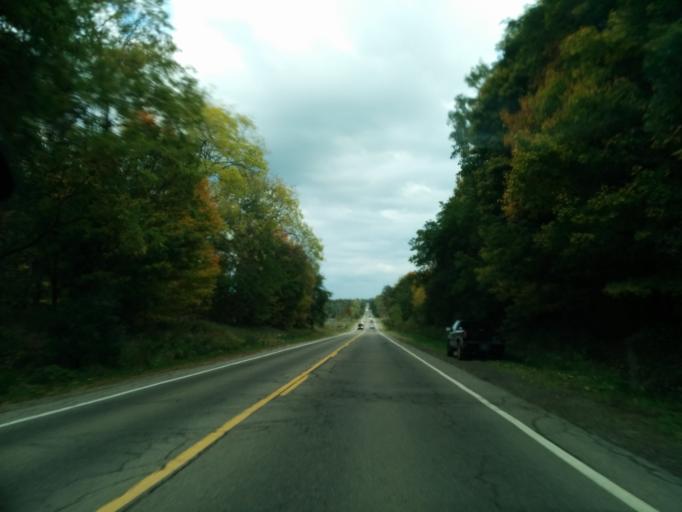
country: US
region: Michigan
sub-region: Oakland County
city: Waterford
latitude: 42.6930
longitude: -83.5081
